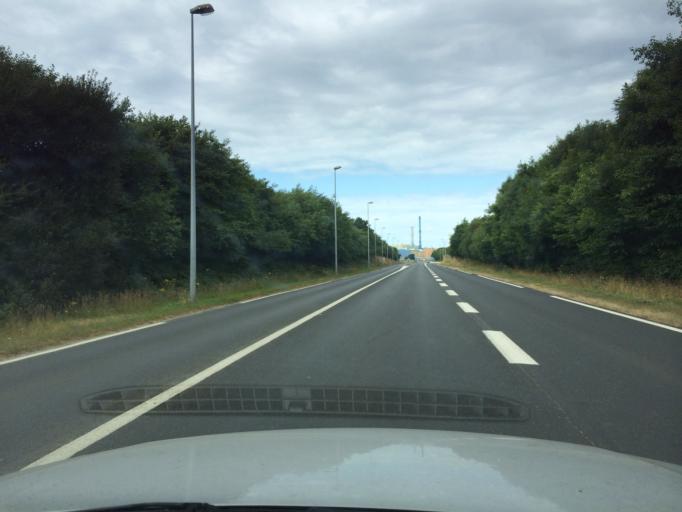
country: FR
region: Lower Normandy
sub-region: Departement de la Manche
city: Beaumont-Hague
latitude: 49.6725
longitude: -1.8605
